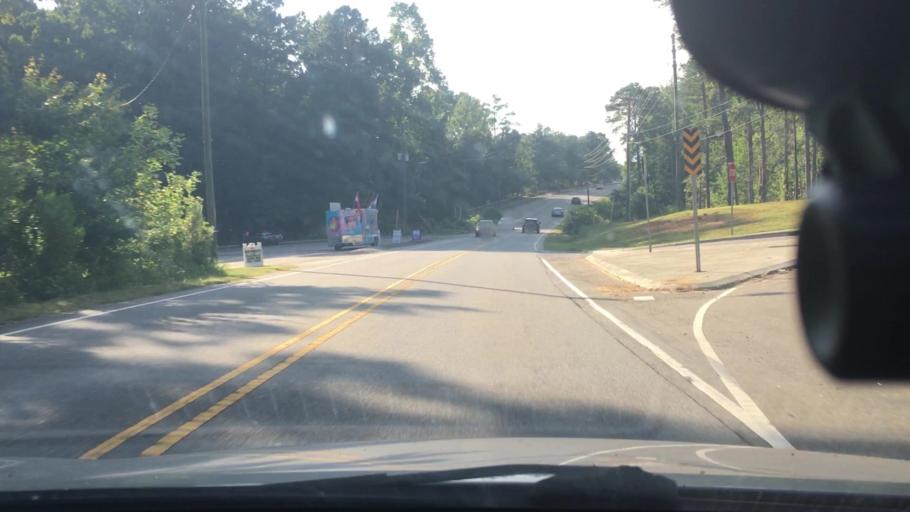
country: US
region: North Carolina
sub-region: Wake County
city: Apex
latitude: 35.7298
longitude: -78.8589
